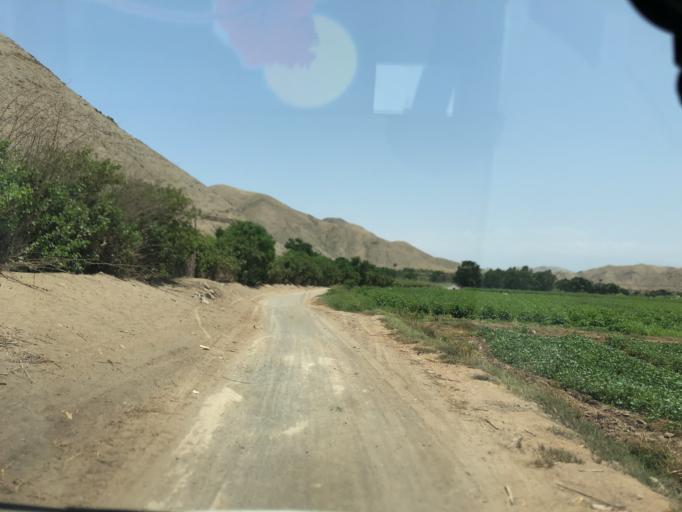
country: PE
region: Lima
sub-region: Provincia de Canete
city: Quilmana
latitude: -12.9872
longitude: -76.4351
